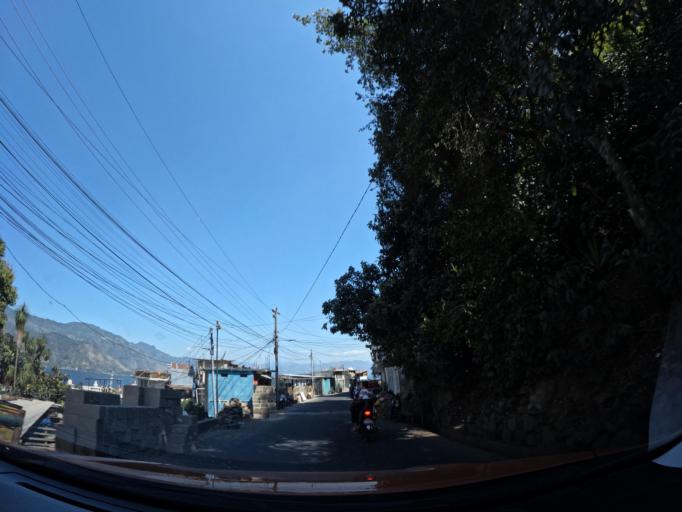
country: GT
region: Solola
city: San Pedro La Laguna
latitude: 14.6901
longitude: -91.2753
